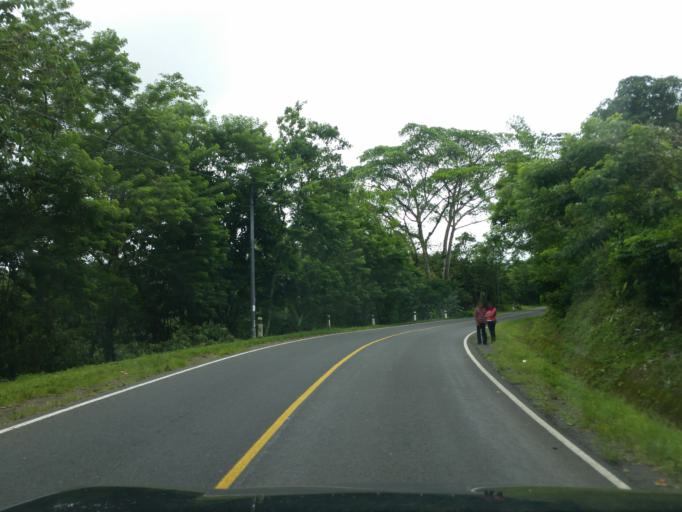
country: NI
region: Matagalpa
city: San Ramon
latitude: 12.9796
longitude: -85.8429
